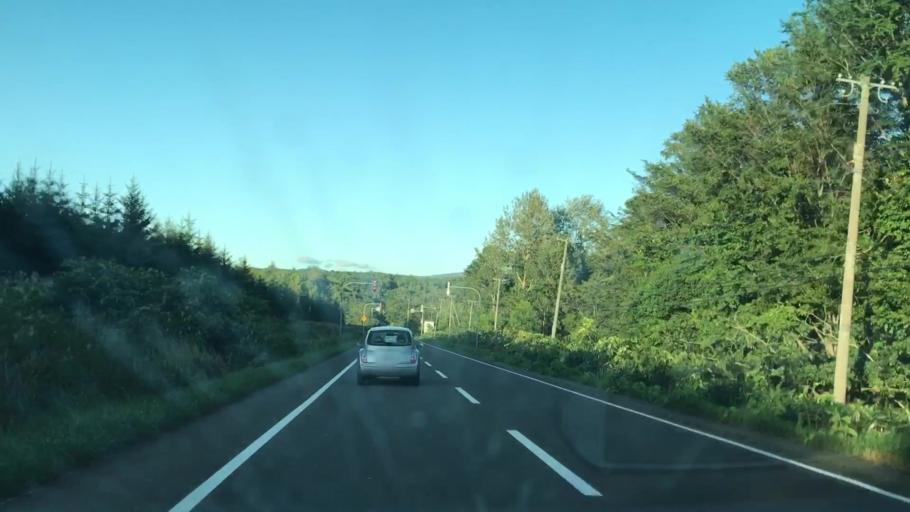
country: JP
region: Hokkaido
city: Niseko Town
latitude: 42.7550
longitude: 140.9217
